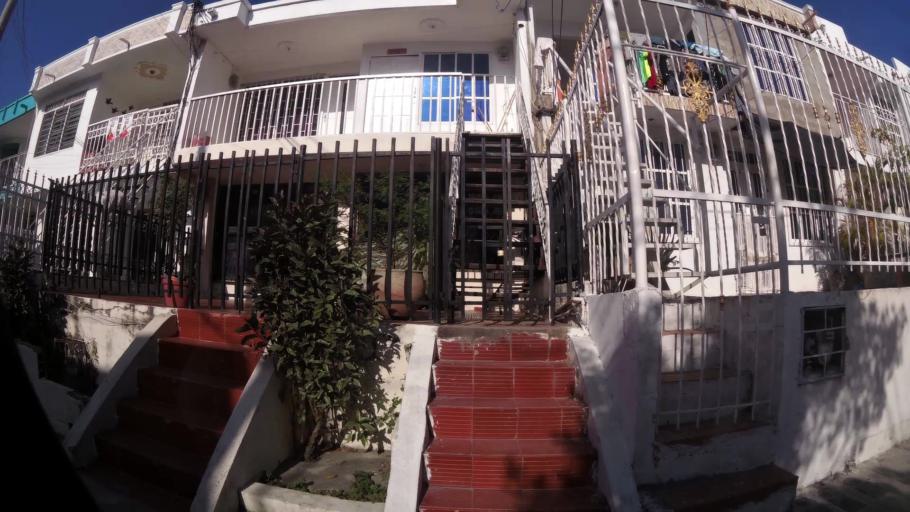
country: CO
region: Bolivar
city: Cartagena
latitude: 10.3954
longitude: -75.4998
